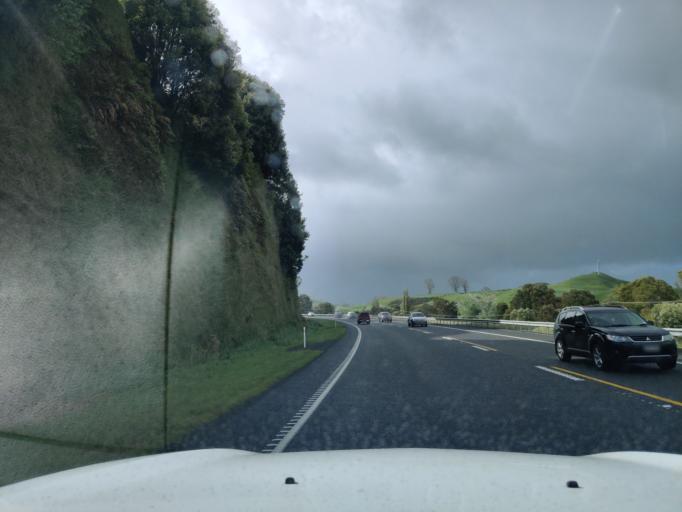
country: NZ
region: Waikato
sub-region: Matamata-Piako District
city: Matamata
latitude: -37.9514
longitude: 175.6752
